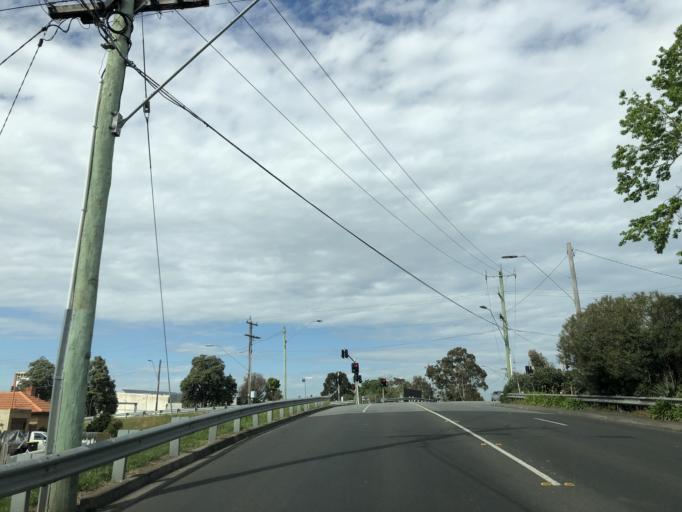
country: AU
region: Victoria
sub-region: Greater Dandenong
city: Dandenong
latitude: -37.9833
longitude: 145.2007
